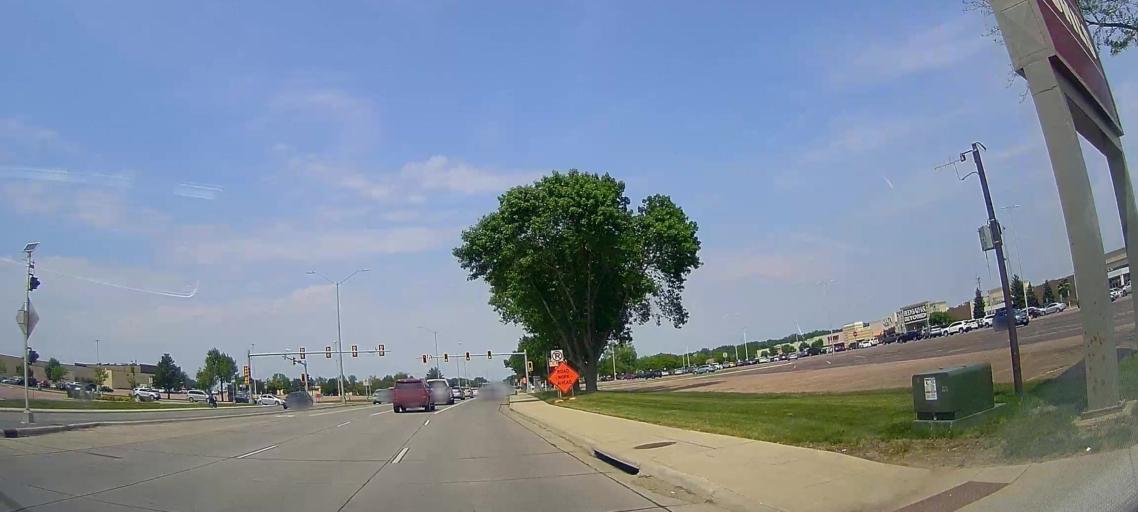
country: US
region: South Dakota
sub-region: Minnehaha County
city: Sioux Falls
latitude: 43.5095
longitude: -96.7709
